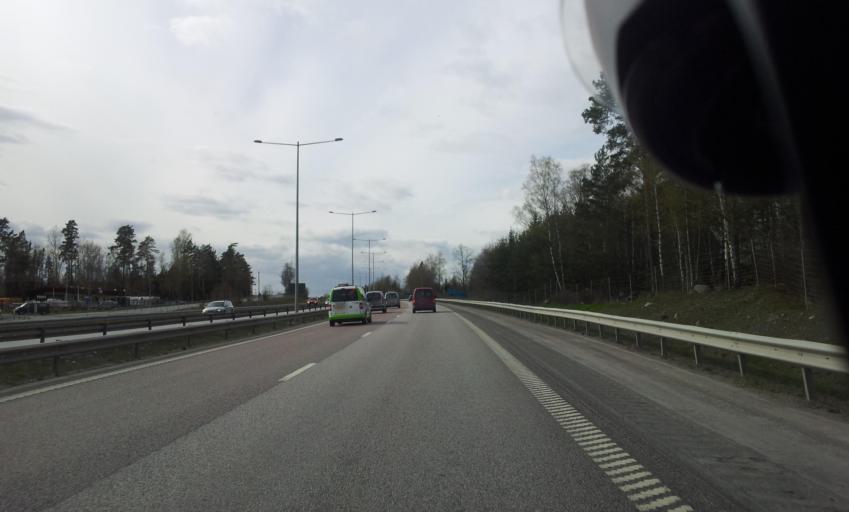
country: SE
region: Stockholm
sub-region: Upplands-Bro Kommun
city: Kungsaengen
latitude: 59.4809
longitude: 17.7823
